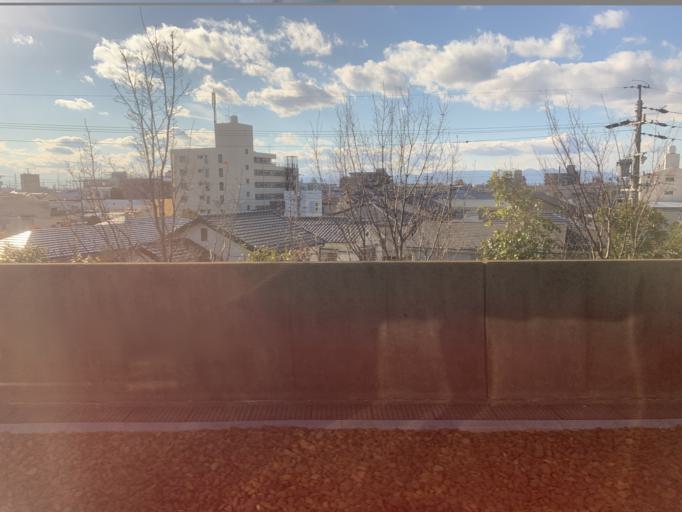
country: JP
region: Aichi
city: Ichinomiya
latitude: 35.2930
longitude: 136.8018
